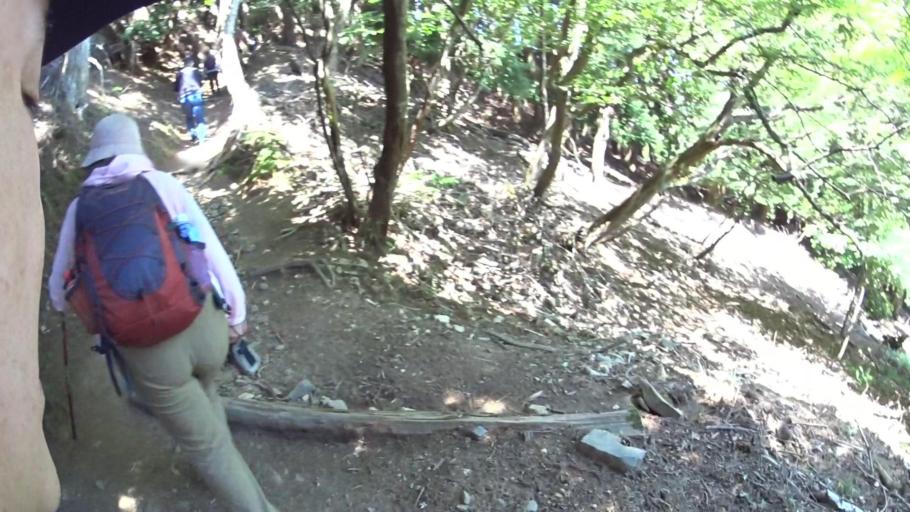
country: JP
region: Kyoto
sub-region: Kyoto-shi
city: Kamigyo-ku
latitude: 35.0614
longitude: 135.8202
